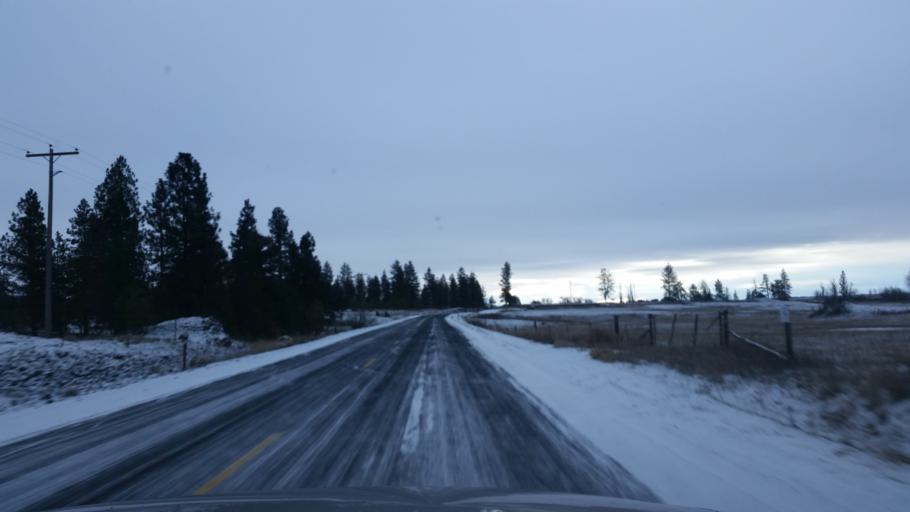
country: US
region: Washington
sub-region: Spokane County
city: Cheney
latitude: 47.4215
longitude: -117.5012
